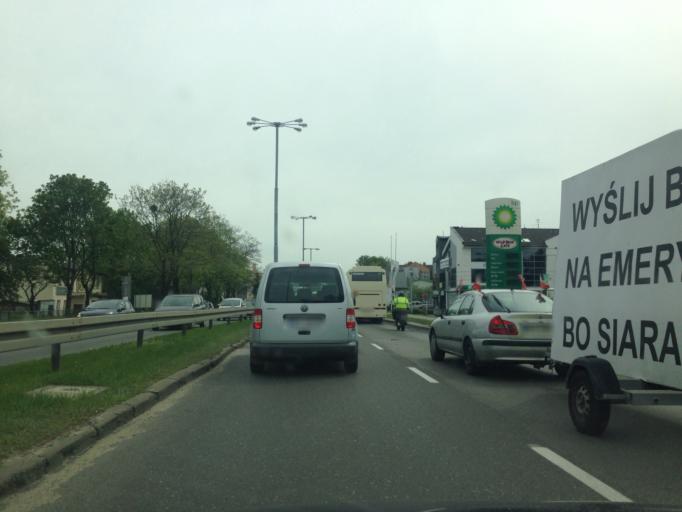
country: PL
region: Pomeranian Voivodeship
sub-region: Sopot
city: Sopot
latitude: 54.4298
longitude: 18.5620
